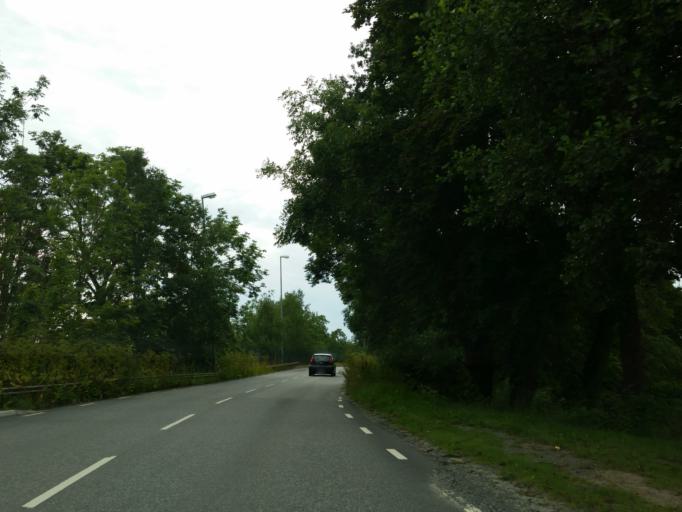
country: SE
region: Stockholm
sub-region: Nykvarns Kommun
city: Nykvarn
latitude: 59.1830
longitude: 17.4329
